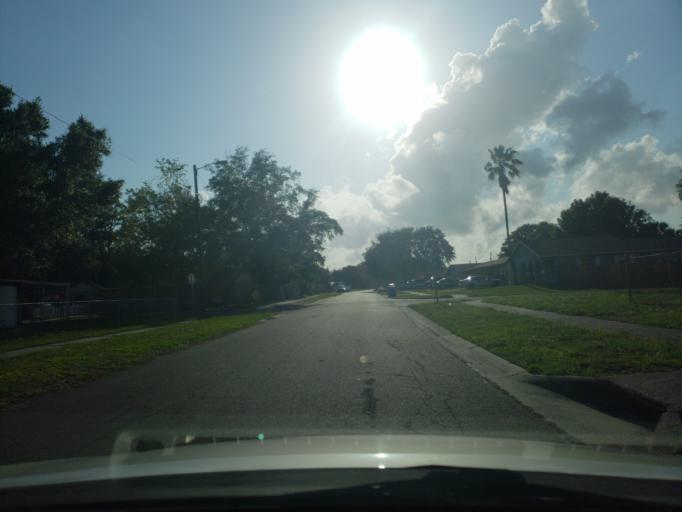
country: US
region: Florida
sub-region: Hillsborough County
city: Palm River-Clair Mel
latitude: 27.9191
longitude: -82.3628
